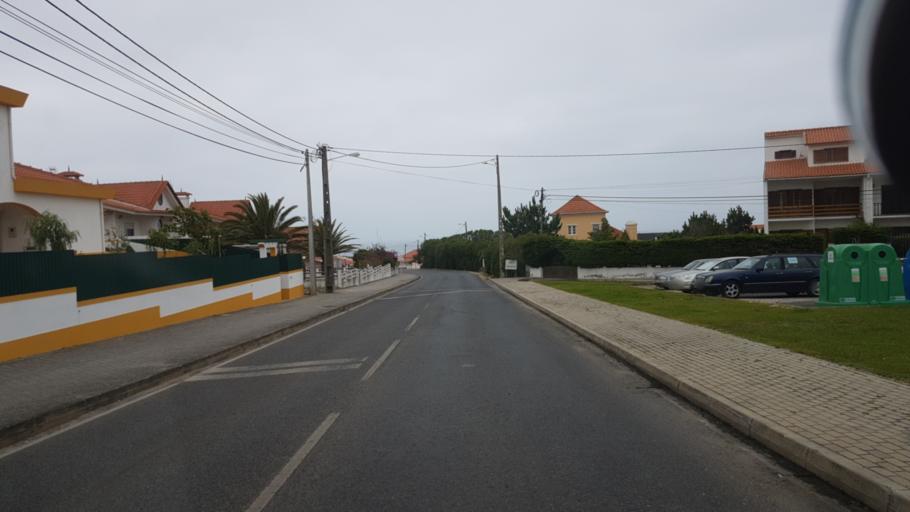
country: PT
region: Lisbon
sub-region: Torres Vedras
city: Silveira
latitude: 39.1442
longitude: -9.3642
